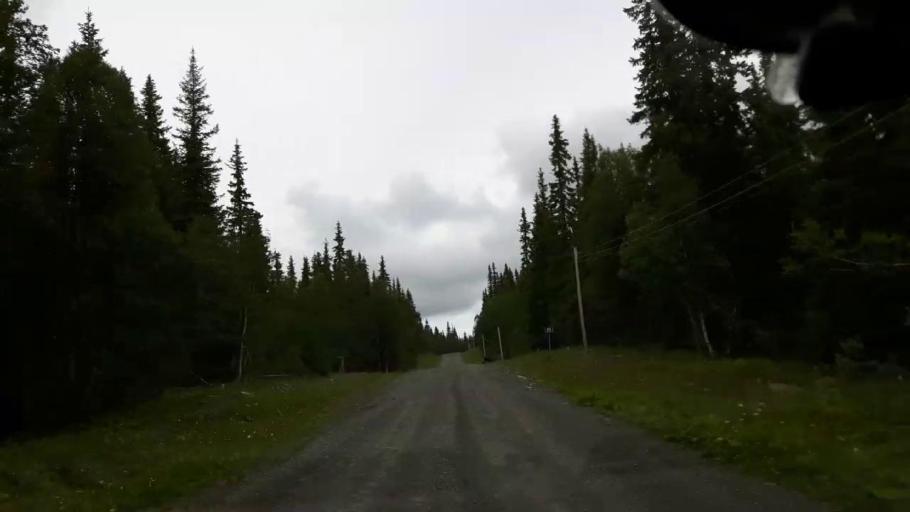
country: SE
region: Jaemtland
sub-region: Krokoms Kommun
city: Valla
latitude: 63.7498
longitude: 13.8355
